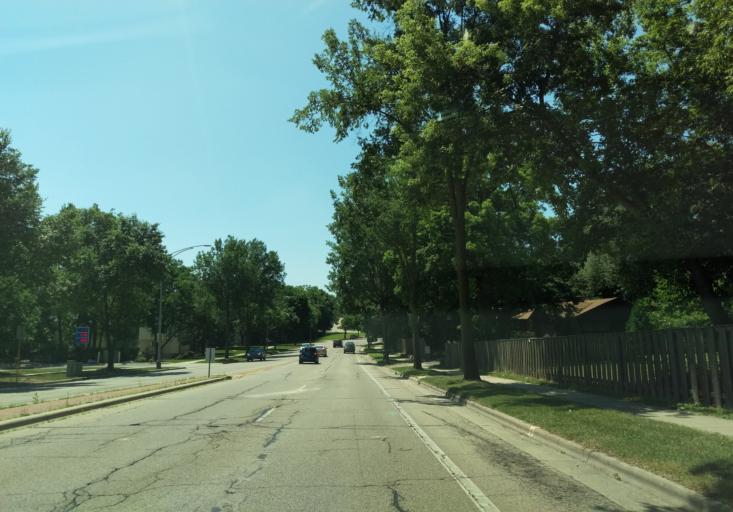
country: US
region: Wisconsin
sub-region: Dane County
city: Middleton
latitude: 43.0462
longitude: -89.5032
